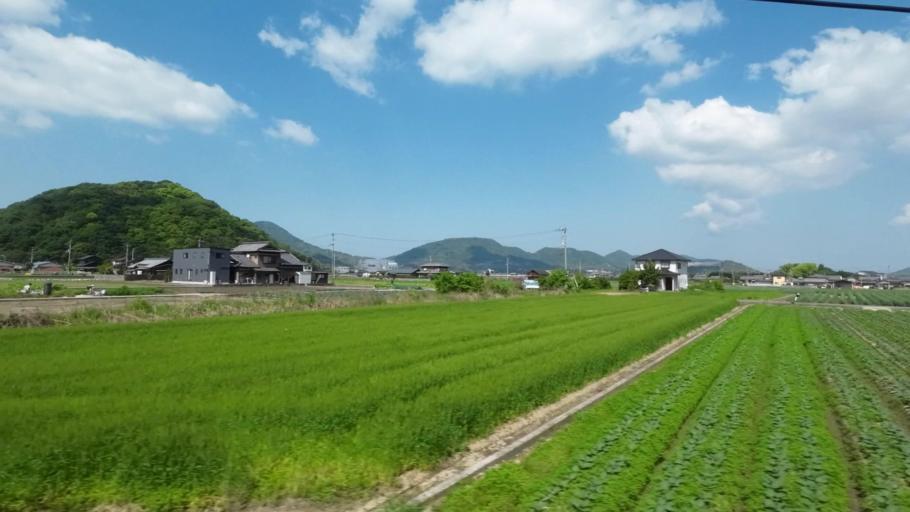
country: JP
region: Kagawa
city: Tadotsu
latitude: 34.1981
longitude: 133.7130
